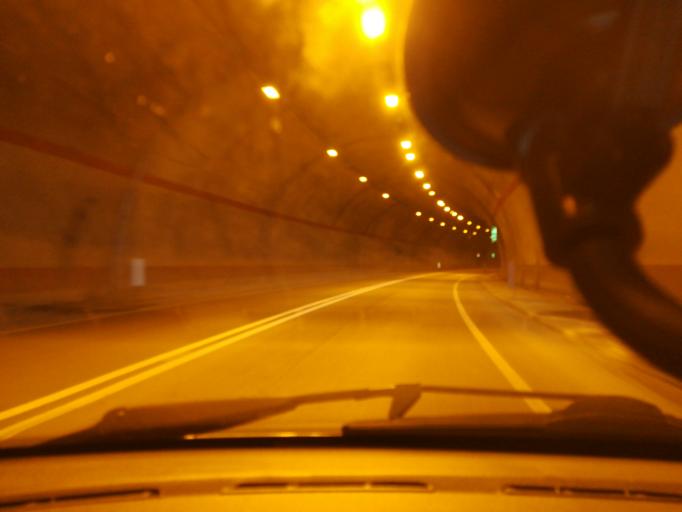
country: IT
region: The Marches
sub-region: Provincia di Macerata
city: Macerata
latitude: 43.3038
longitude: 13.4431
